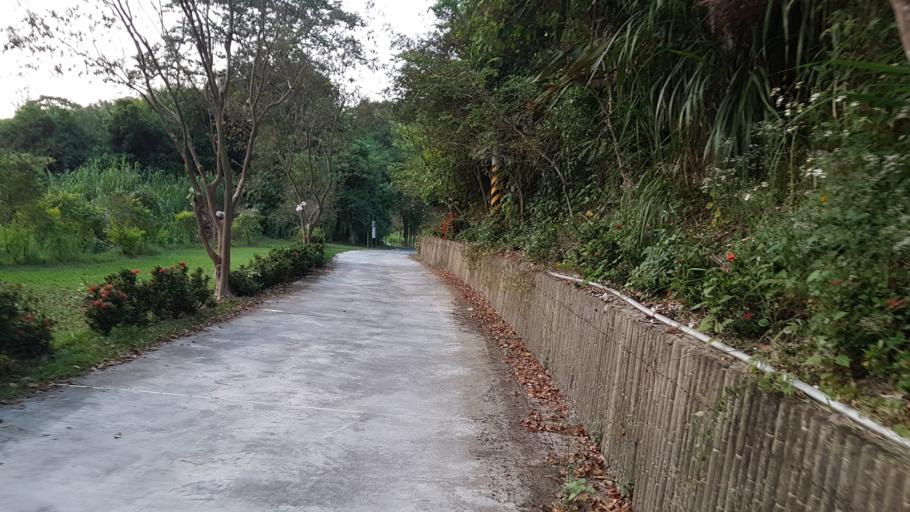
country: TW
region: Taiwan
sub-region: Chiayi
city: Jiayi Shi
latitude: 23.3614
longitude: 120.4683
